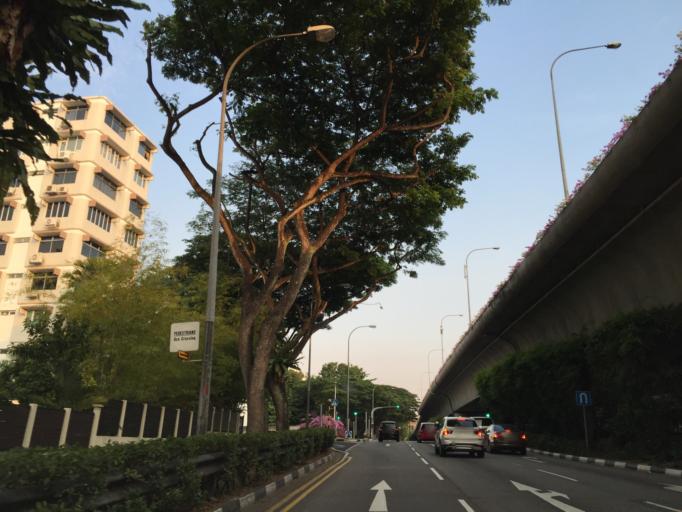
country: SG
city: Singapore
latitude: 1.3104
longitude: 103.8044
